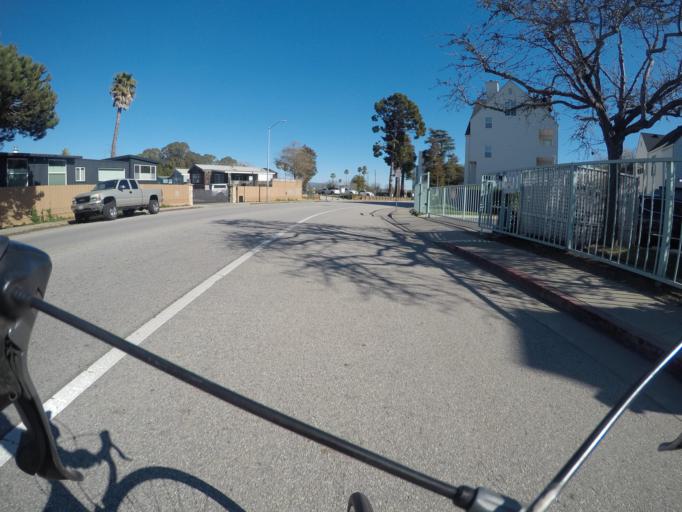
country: US
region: California
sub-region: Santa Cruz County
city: Santa Cruz
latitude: 36.9613
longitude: -122.0271
